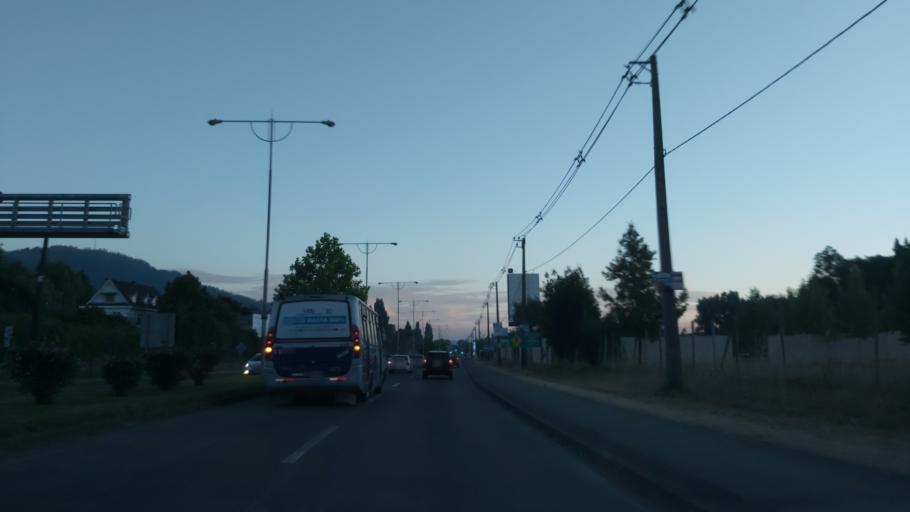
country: CL
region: Biobio
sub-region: Provincia de Concepcion
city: Chiguayante
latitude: -36.8967
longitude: -73.0332
